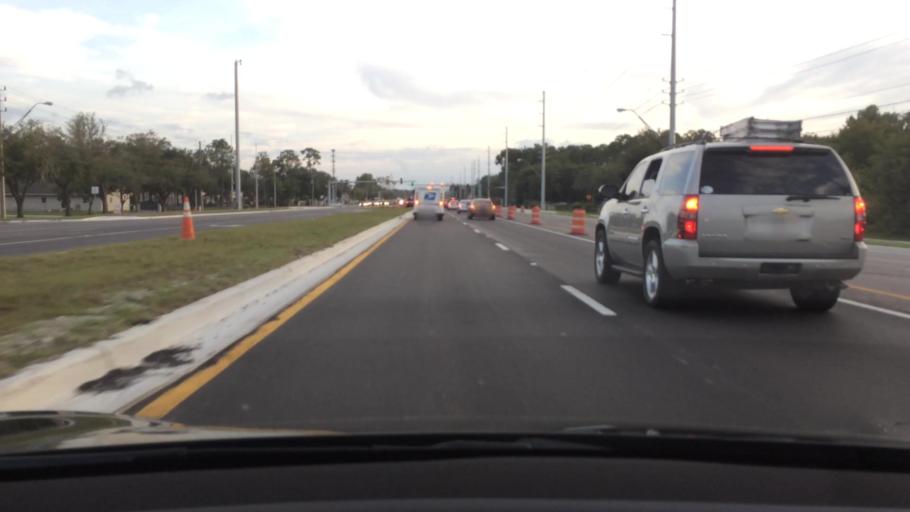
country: US
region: Florida
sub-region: Hillsborough County
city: Pebble Creek
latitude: 28.1564
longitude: -82.3535
